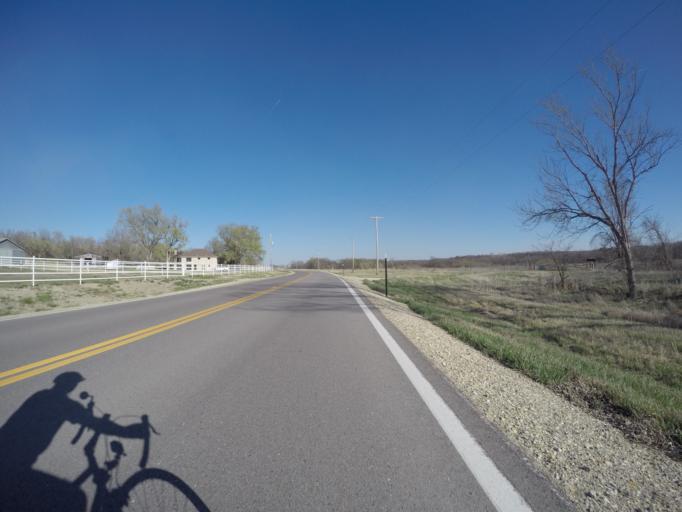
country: US
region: Kansas
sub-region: Riley County
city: Ogden
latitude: 39.2332
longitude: -96.7551
